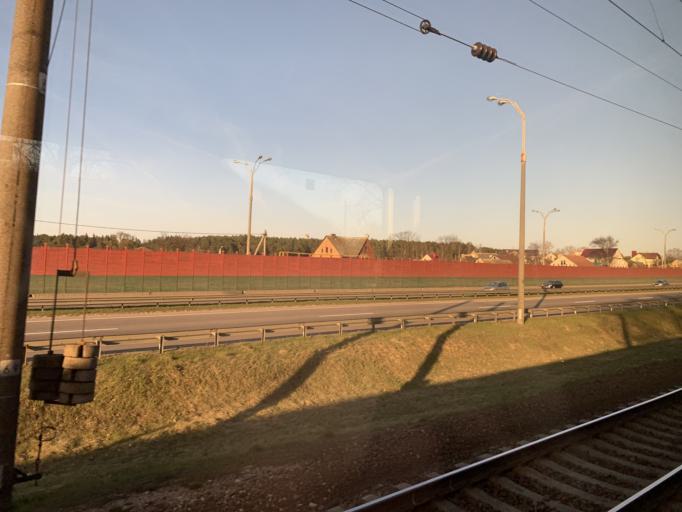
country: BY
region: Minsk
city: Zhdanovichy
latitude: 53.9507
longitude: 27.4158
